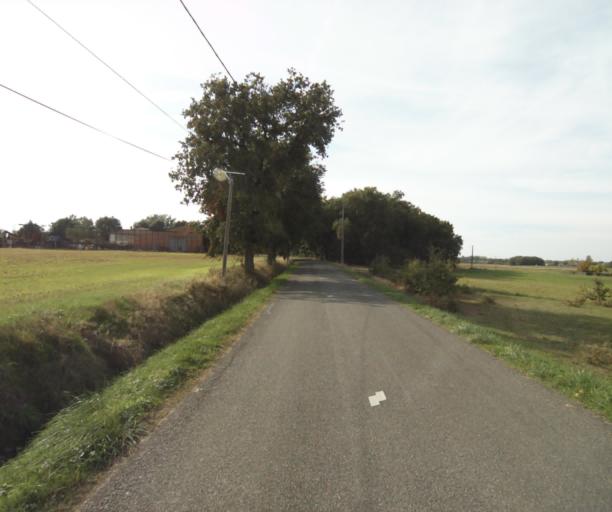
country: FR
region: Midi-Pyrenees
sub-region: Departement du Tarn-et-Garonne
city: Labastide-Saint-Pierre
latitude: 43.9085
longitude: 1.3867
